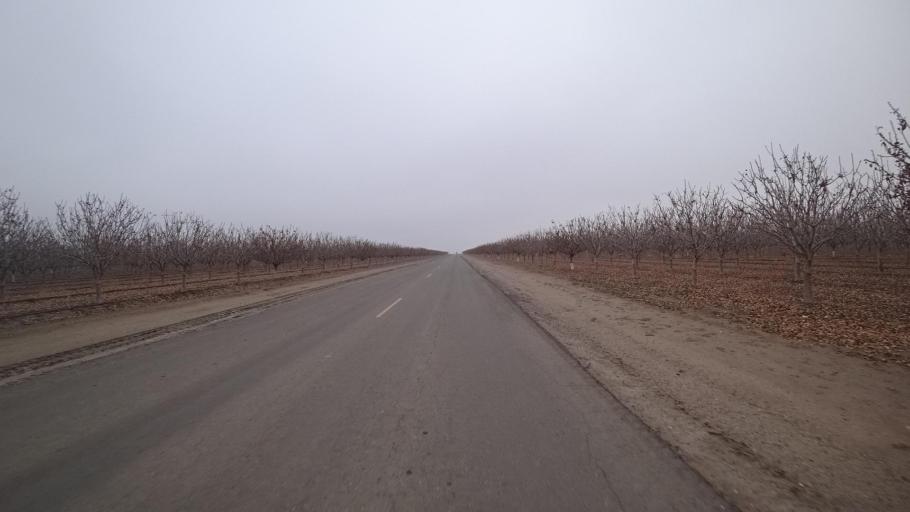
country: US
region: California
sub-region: Kern County
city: Rosedale
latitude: 35.2052
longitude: -119.2329
